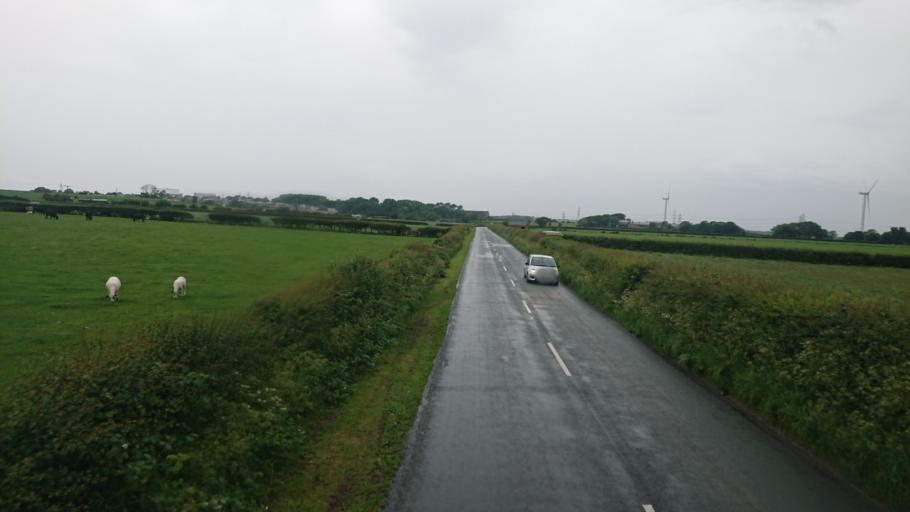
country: GB
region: England
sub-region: Lancashire
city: Morecambe
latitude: 54.0182
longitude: -2.8671
